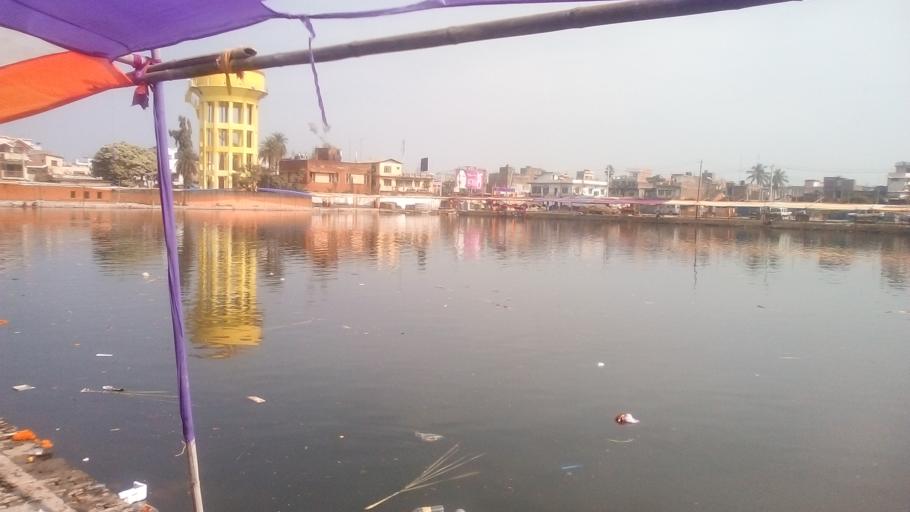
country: NP
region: Central Region
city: Janakpur
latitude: 26.7317
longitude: 85.9247
